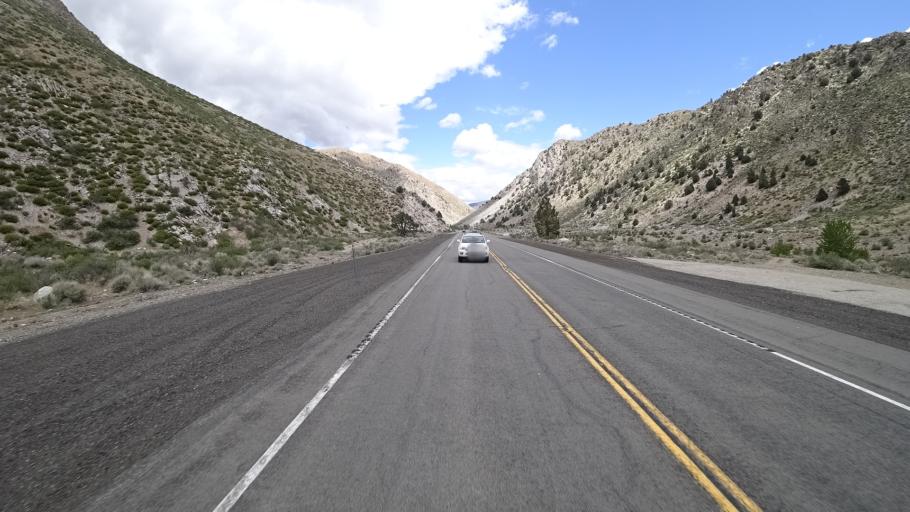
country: US
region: Nevada
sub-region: Lyon County
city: Smith Valley
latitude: 38.4888
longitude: -119.4564
